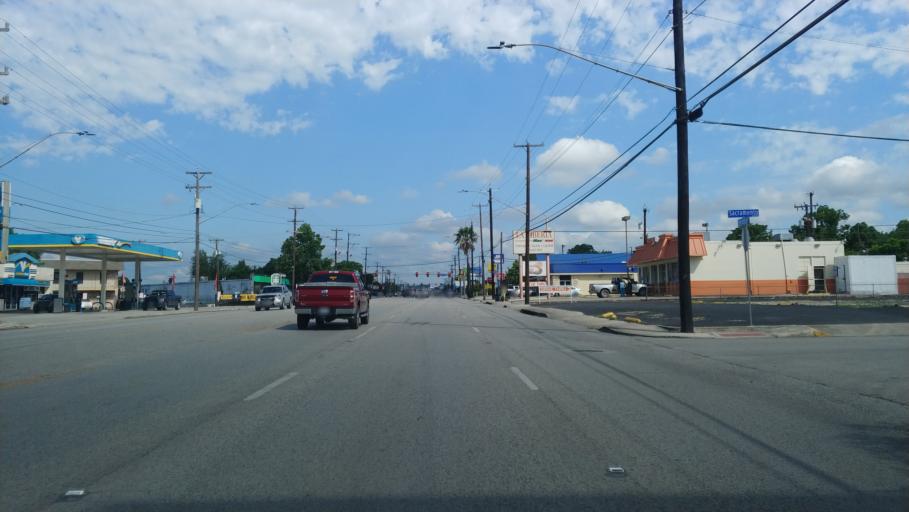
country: US
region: Texas
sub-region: Bexar County
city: Balcones Heights
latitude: 29.4707
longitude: -98.5321
